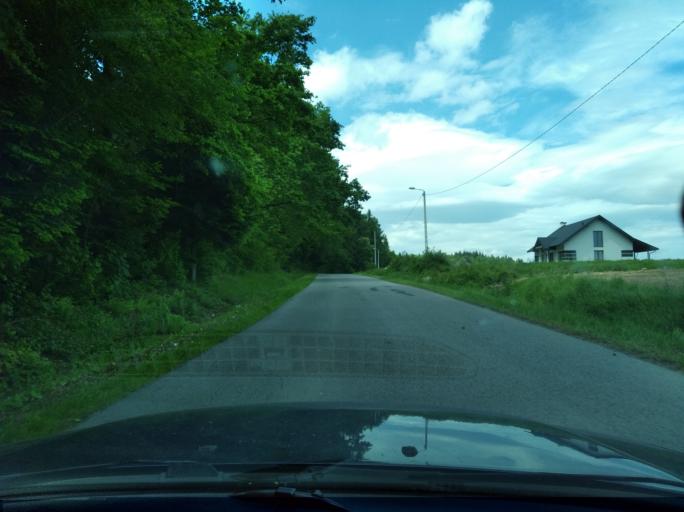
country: PL
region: Subcarpathian Voivodeship
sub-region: Powiat ropczycko-sedziszowski
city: Ropczyce
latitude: 50.0072
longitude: 21.6138
